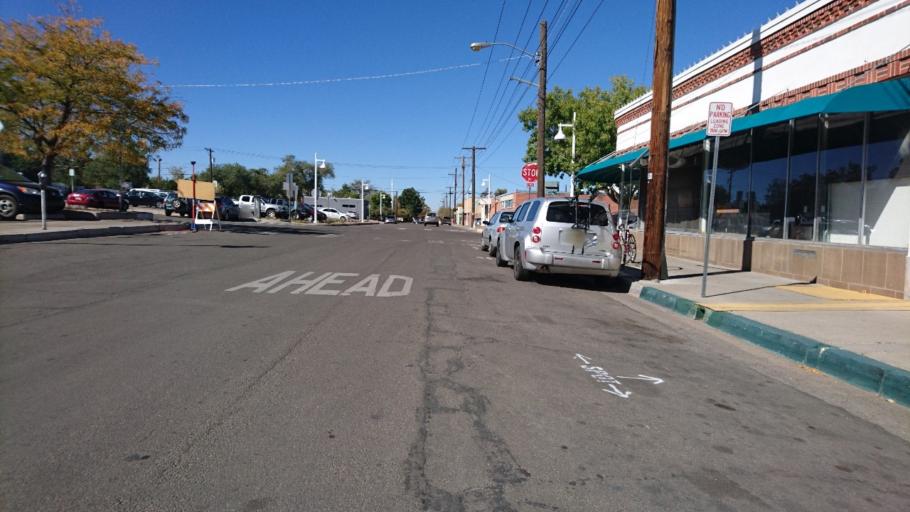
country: US
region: New Mexico
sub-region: Bernalillo County
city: Albuquerque
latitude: 35.0791
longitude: -106.6054
